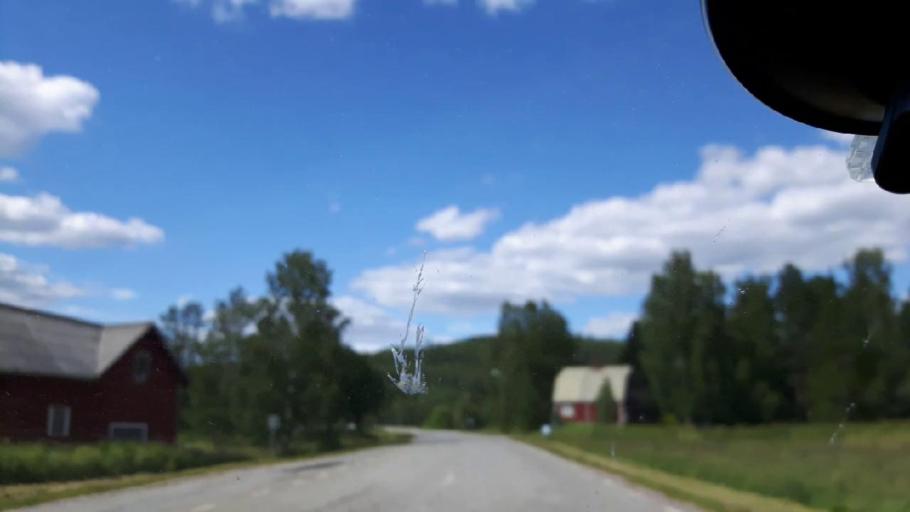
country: SE
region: Vaesternorrland
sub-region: Ange Kommun
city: Fransta
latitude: 62.7865
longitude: 16.2433
